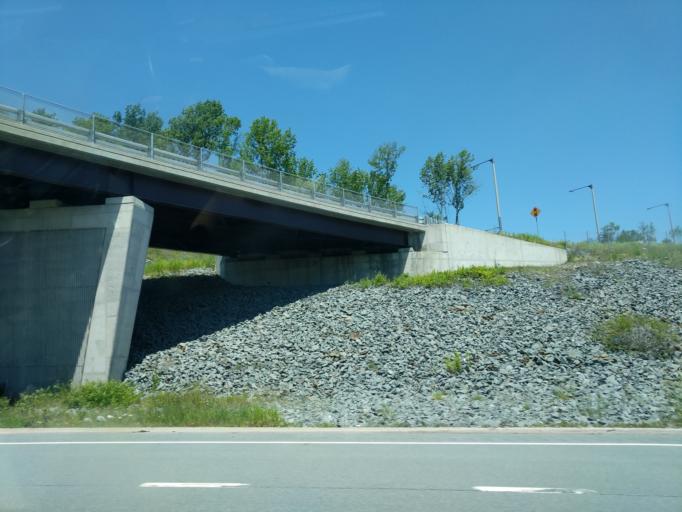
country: US
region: New York
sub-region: Sullivan County
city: Monticello
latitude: 41.6446
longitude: -74.6488
